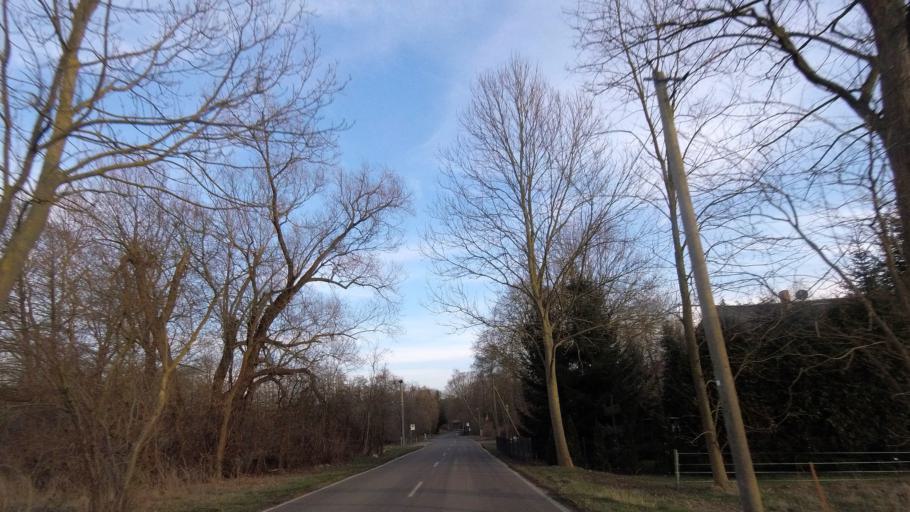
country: DE
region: Brandenburg
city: Niemegk
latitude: 52.0755
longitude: 12.6574
